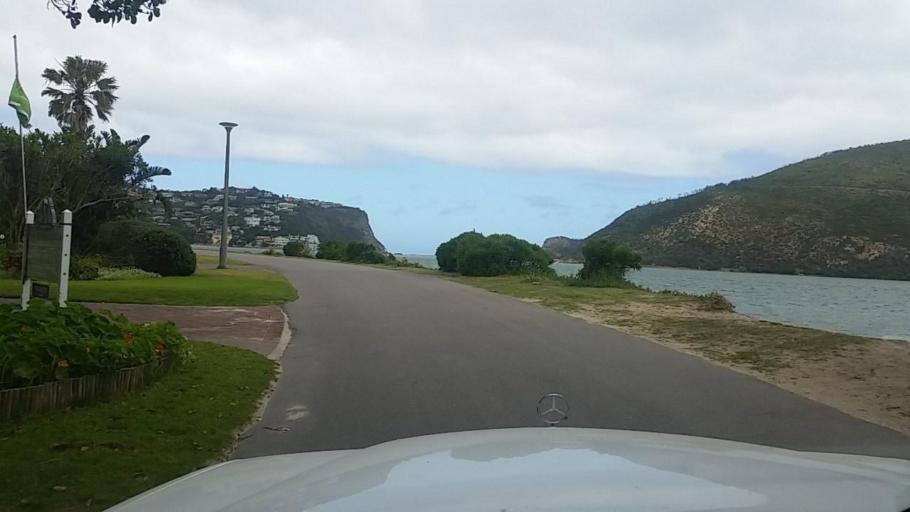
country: ZA
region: Western Cape
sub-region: Eden District Municipality
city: Knysna
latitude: -34.0673
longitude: 23.0557
